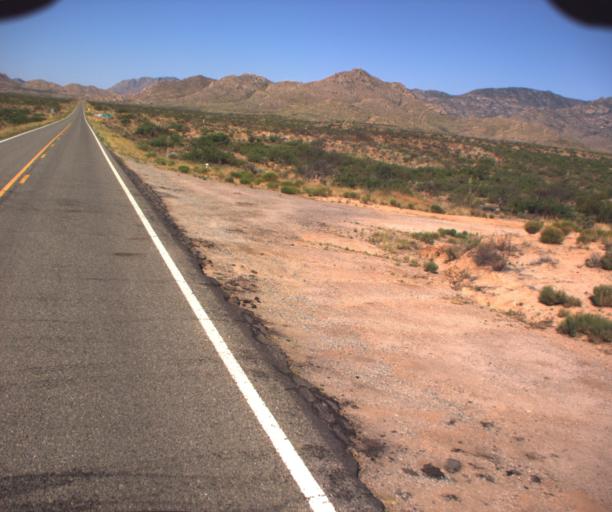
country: US
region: Arizona
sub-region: Graham County
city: Swift Trail Junction
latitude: 32.5966
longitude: -109.6872
